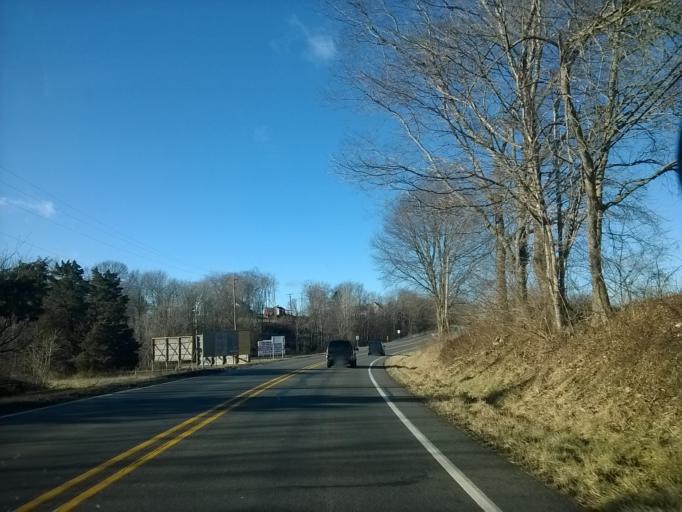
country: US
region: Indiana
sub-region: Jefferson County
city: Hanover
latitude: 38.7092
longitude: -85.5226
